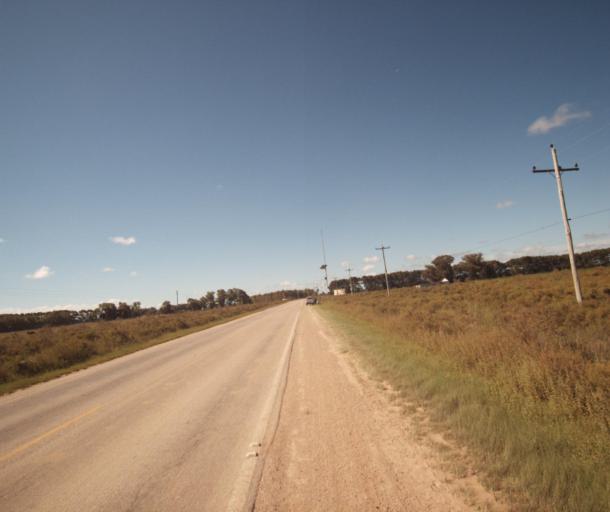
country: BR
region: Rio Grande do Sul
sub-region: Santa Vitoria Do Palmar
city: Santa Vitoria do Palmar
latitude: -33.5619
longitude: -53.3716
